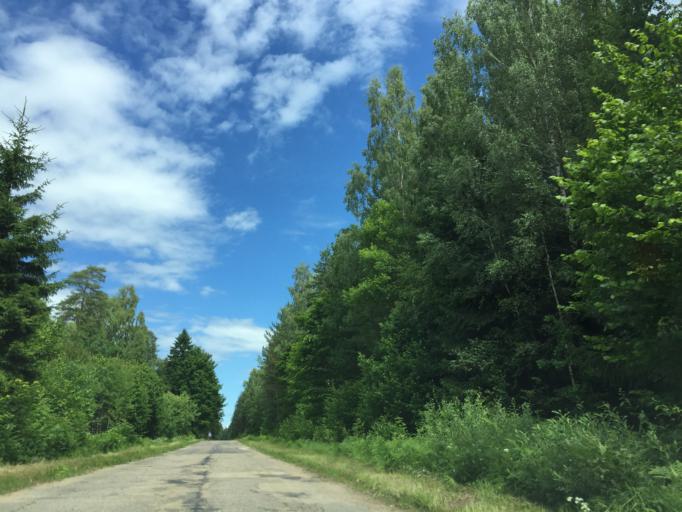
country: LV
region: Saulkrastu
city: Saulkrasti
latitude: 57.4109
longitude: 24.4241
